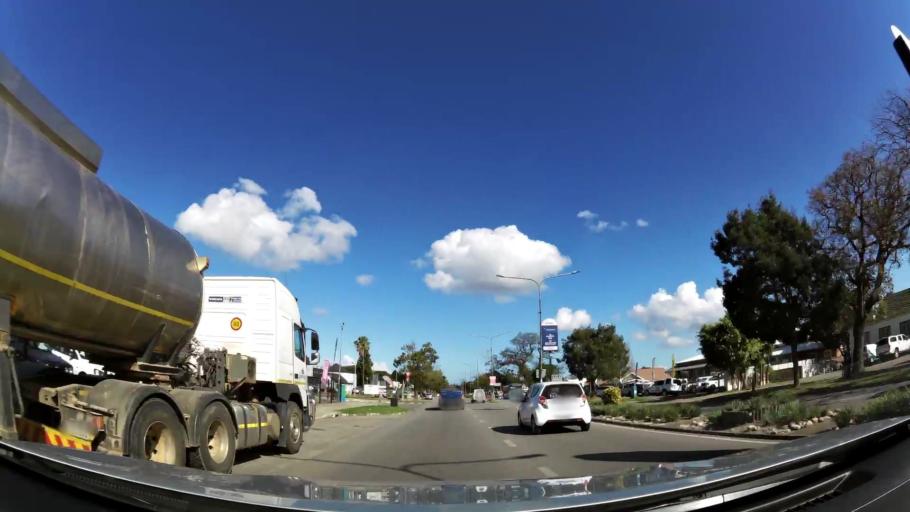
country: ZA
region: Western Cape
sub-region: Eden District Municipality
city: George
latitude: -33.9651
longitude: 22.4519
